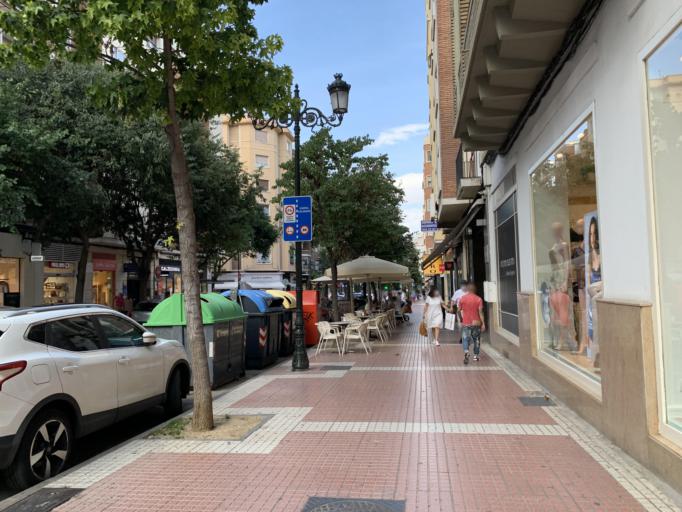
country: ES
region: Aragon
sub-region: Provincia de Zaragoza
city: Zaragoza
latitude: 41.6450
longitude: -0.8840
